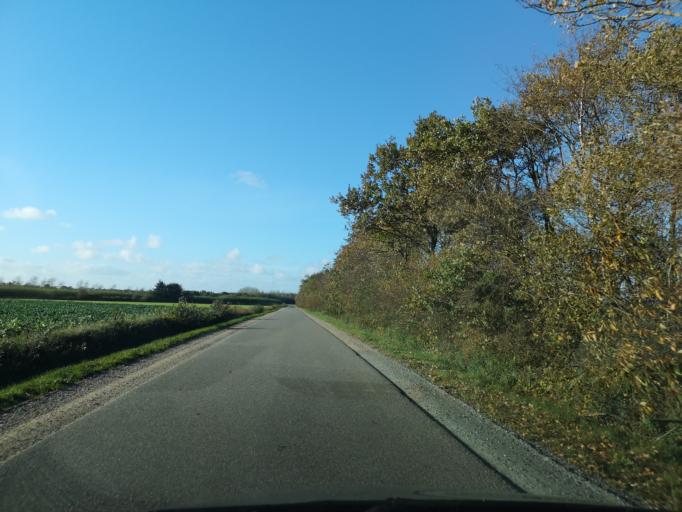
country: DK
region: Central Jutland
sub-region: Ringkobing-Skjern Kommune
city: Tarm
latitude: 55.8135
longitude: 8.4333
